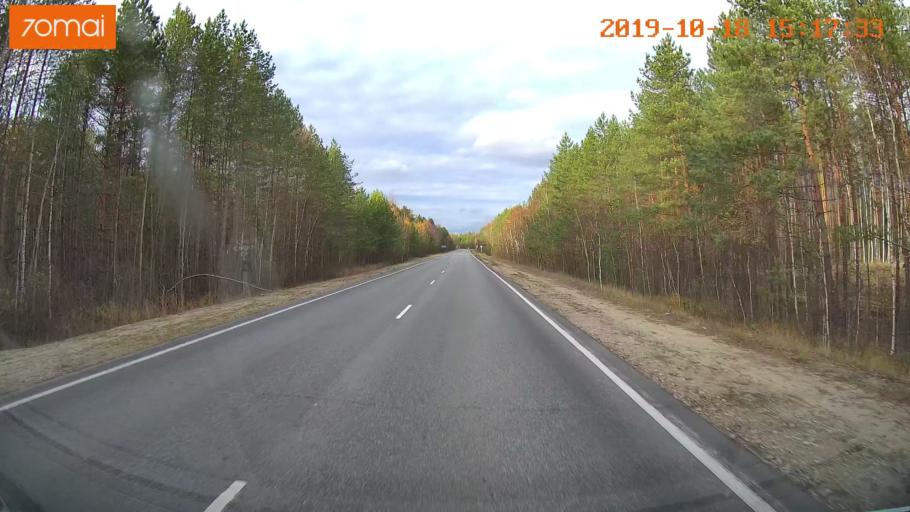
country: RU
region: Vladimir
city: Anopino
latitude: 55.6515
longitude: 40.7268
